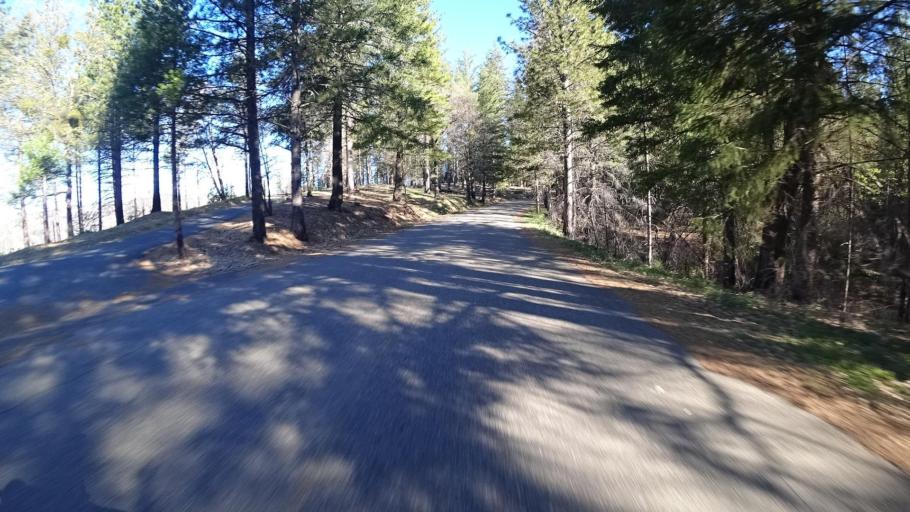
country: US
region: California
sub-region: Lake County
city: Upper Lake
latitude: 39.2987
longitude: -122.9288
